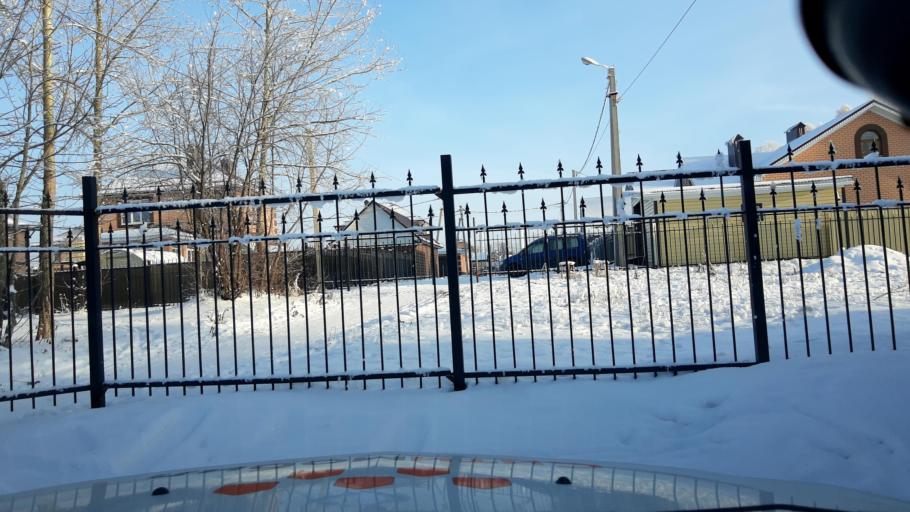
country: RU
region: Bashkortostan
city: Mikhaylovka
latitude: 54.8291
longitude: 55.8726
